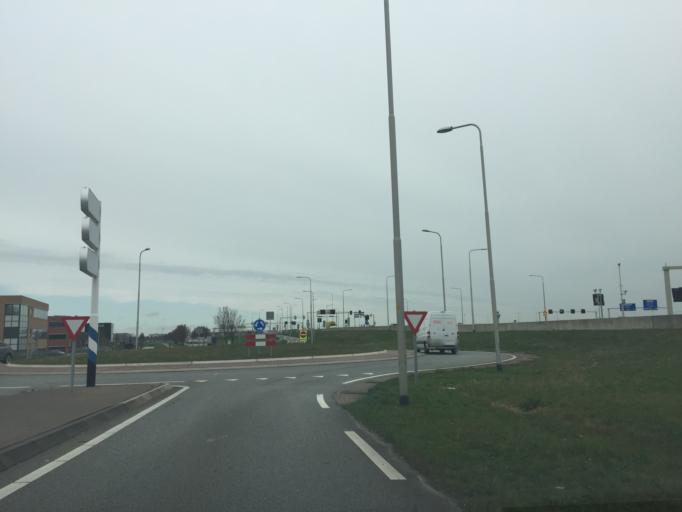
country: NL
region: North Holland
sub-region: Gemeente Aalsmeer
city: Aalsmeer
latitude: 52.2829
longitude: 4.7744
